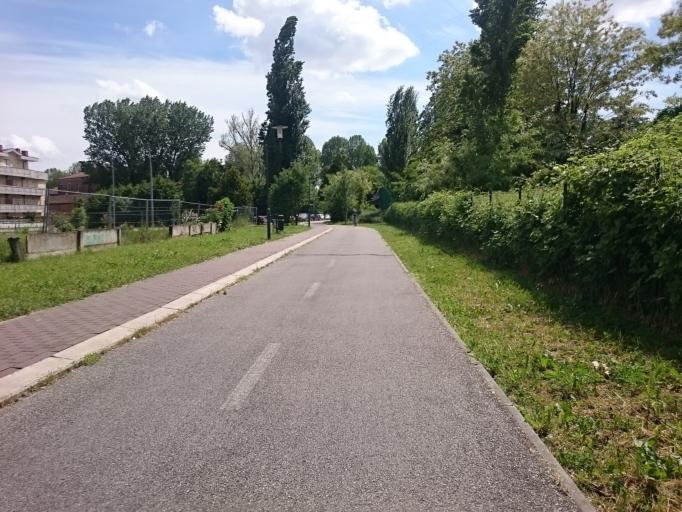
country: IT
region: Veneto
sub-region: Provincia di Rovigo
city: Rovigo
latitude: 45.0785
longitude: 11.7826
